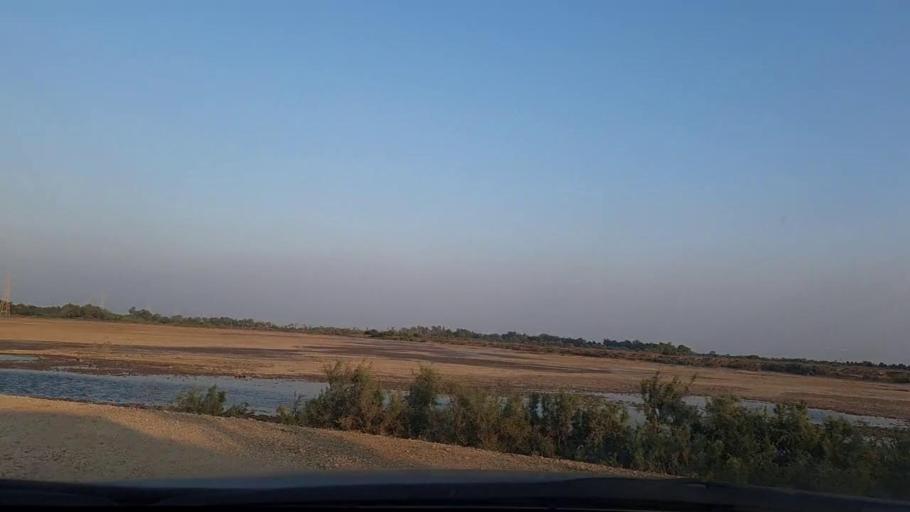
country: PK
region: Sindh
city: Mirpur Sakro
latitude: 24.5606
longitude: 67.6599
